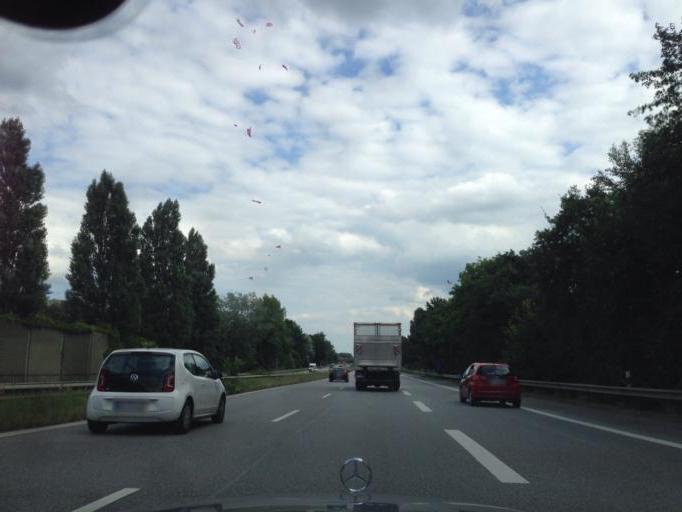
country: DE
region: Hamburg
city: Marienthal
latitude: 53.5426
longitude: 10.0893
